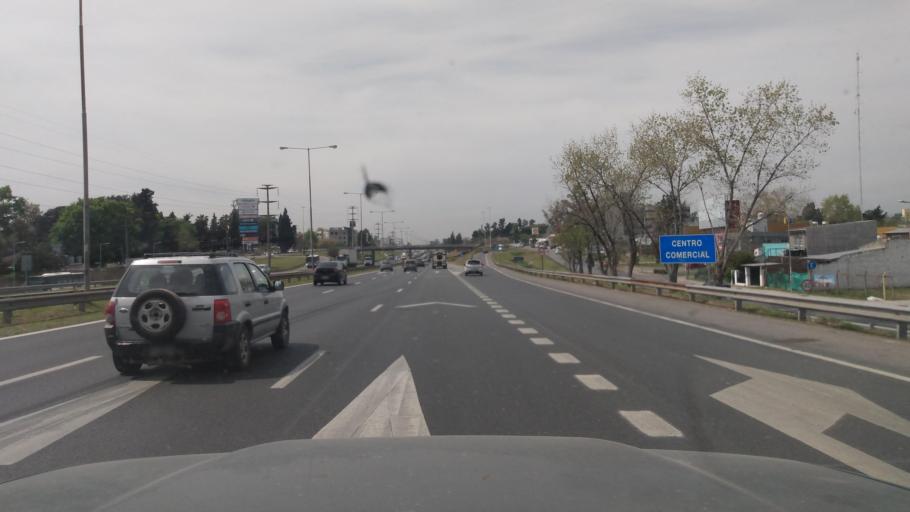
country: AR
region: Buenos Aires
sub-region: Partido de Pilar
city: Pilar
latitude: -34.4517
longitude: -58.9203
